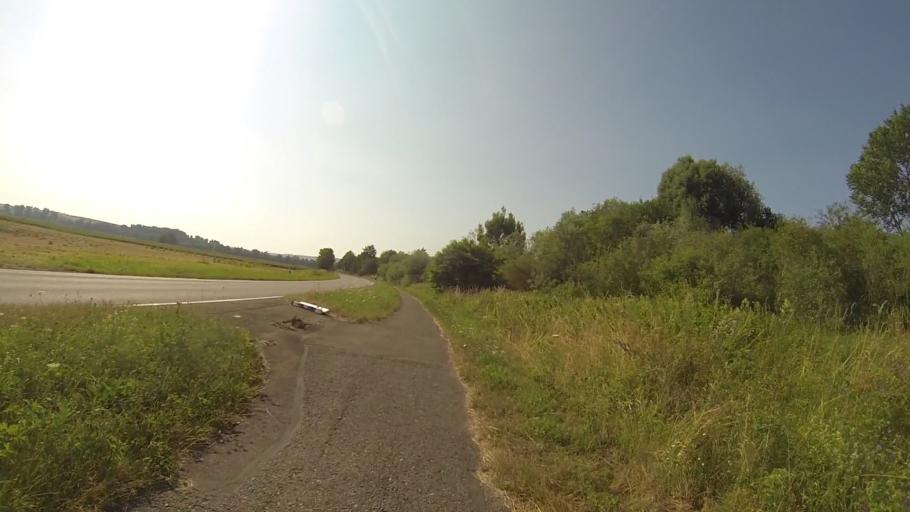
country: DE
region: Baden-Wuerttemberg
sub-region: Tuebingen Region
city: Erbach
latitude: 48.3484
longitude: 9.9336
